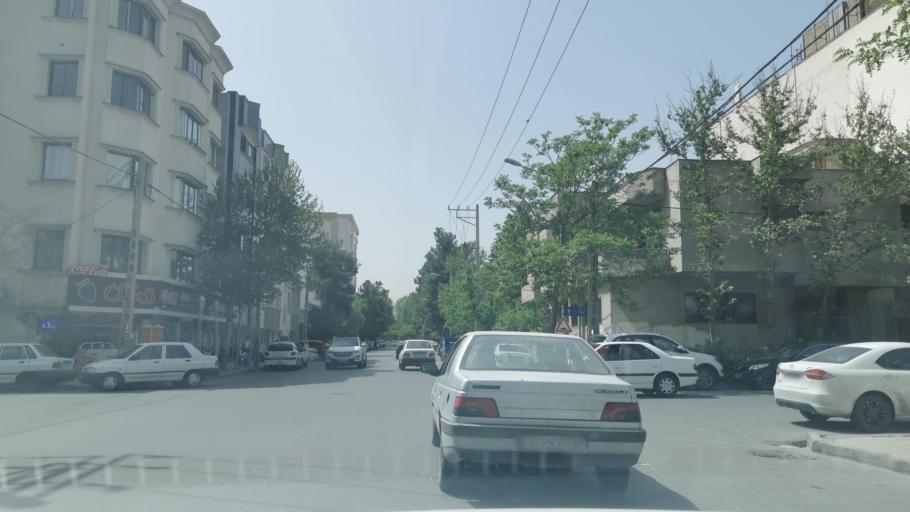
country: IR
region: Razavi Khorasan
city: Mashhad
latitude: 36.3055
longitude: 59.5588
